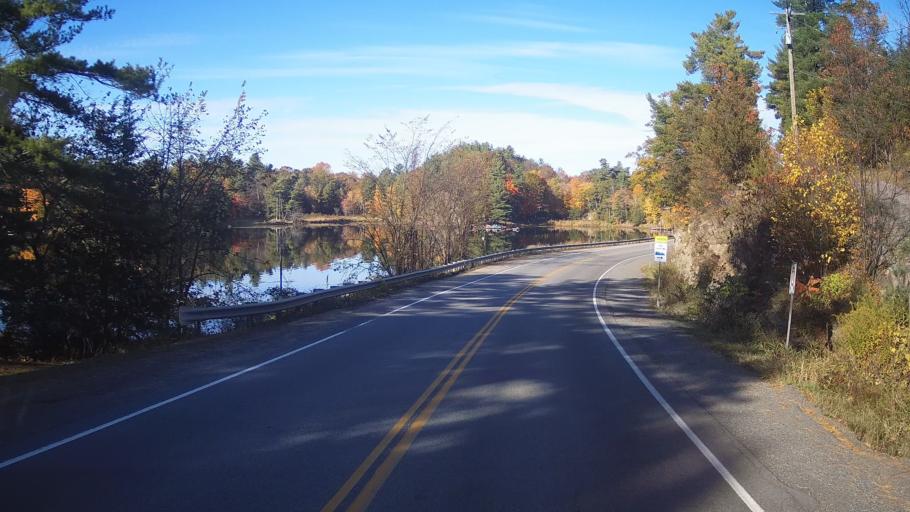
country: CA
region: Ontario
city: Kingston
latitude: 44.5402
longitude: -76.4434
